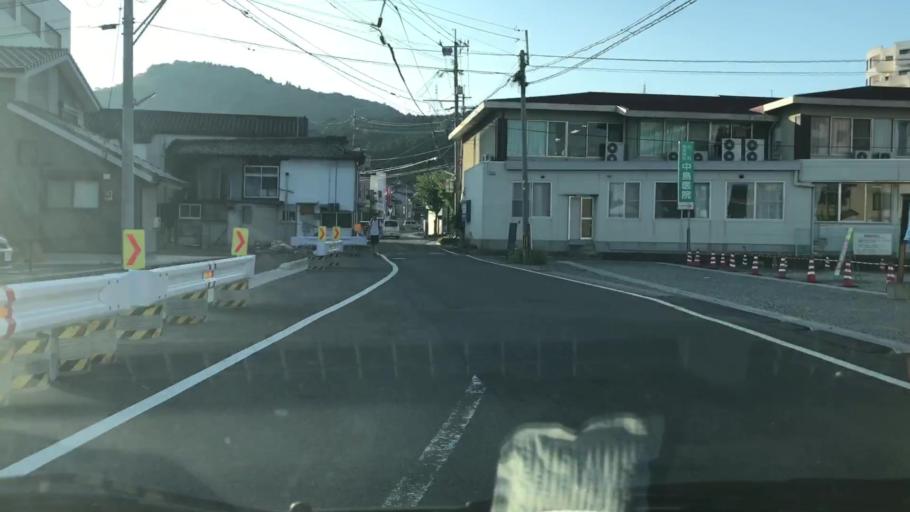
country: JP
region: Saga Prefecture
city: Takeocho-takeo
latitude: 33.1954
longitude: 130.0200
